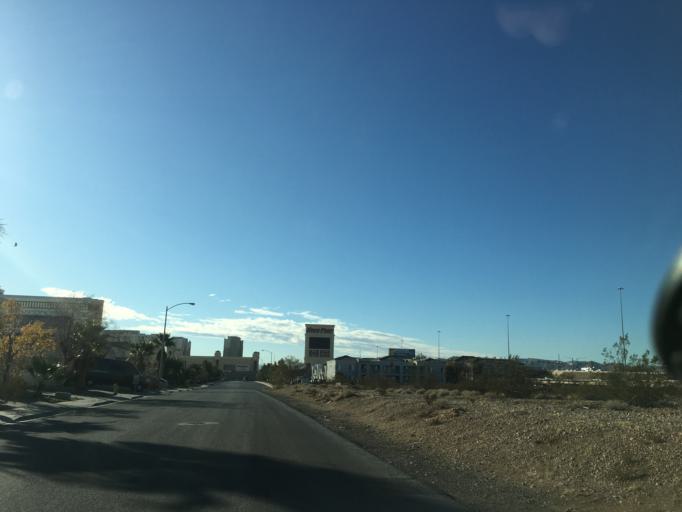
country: US
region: Nevada
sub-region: Clark County
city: Enterprise
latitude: 36.0166
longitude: -115.1788
